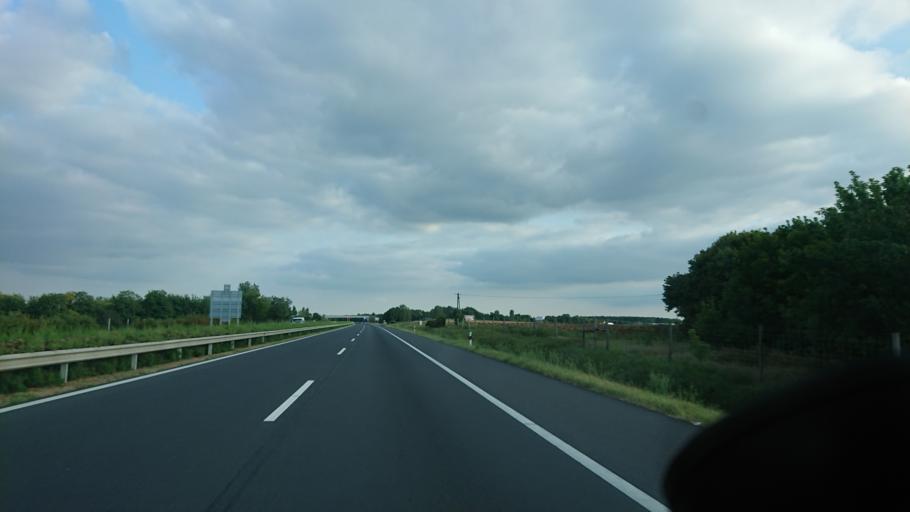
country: HU
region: Bacs-Kiskun
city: Kiskunfelegyhaza
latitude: 46.7082
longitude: 19.7988
